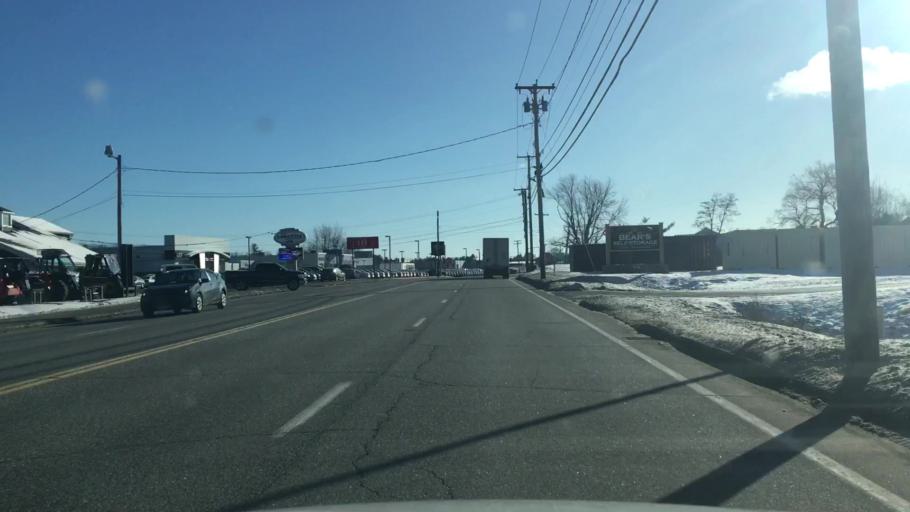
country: US
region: Maine
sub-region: Androscoggin County
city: Lewiston
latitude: 44.1320
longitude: -70.2253
